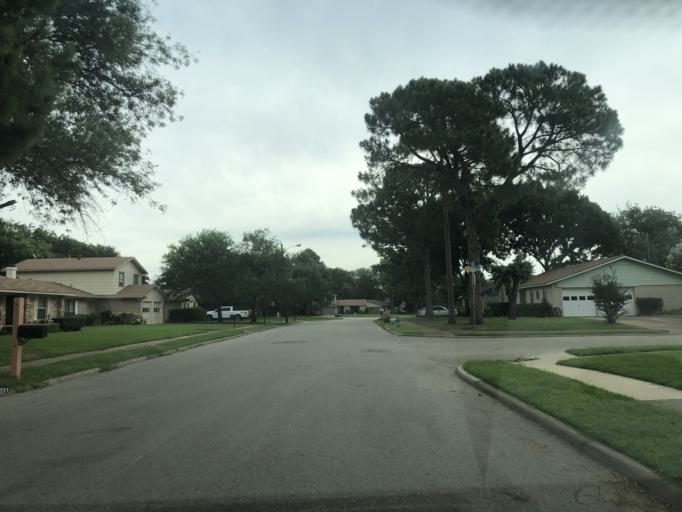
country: US
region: Texas
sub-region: Dallas County
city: Irving
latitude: 32.7859
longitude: -96.9718
